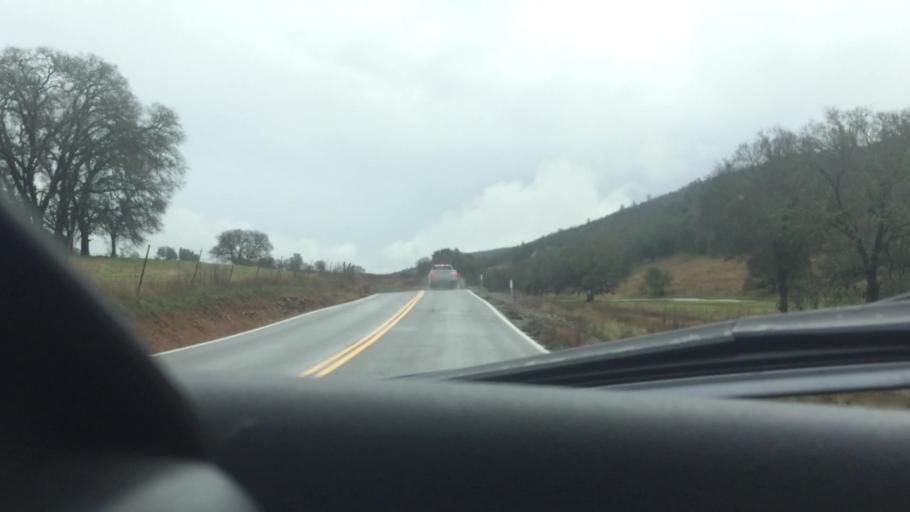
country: US
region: California
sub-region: El Dorado County
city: Cameron Park
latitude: 38.5956
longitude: -121.0181
